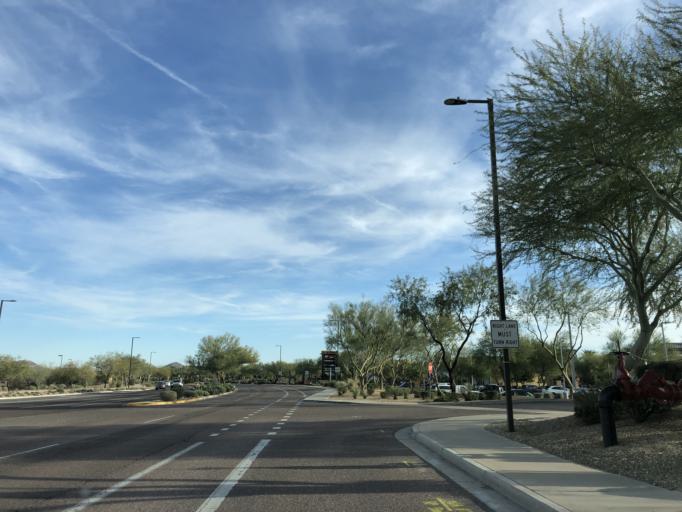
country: US
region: Arizona
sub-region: Maricopa County
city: Anthem
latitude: 33.7169
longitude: -112.1138
